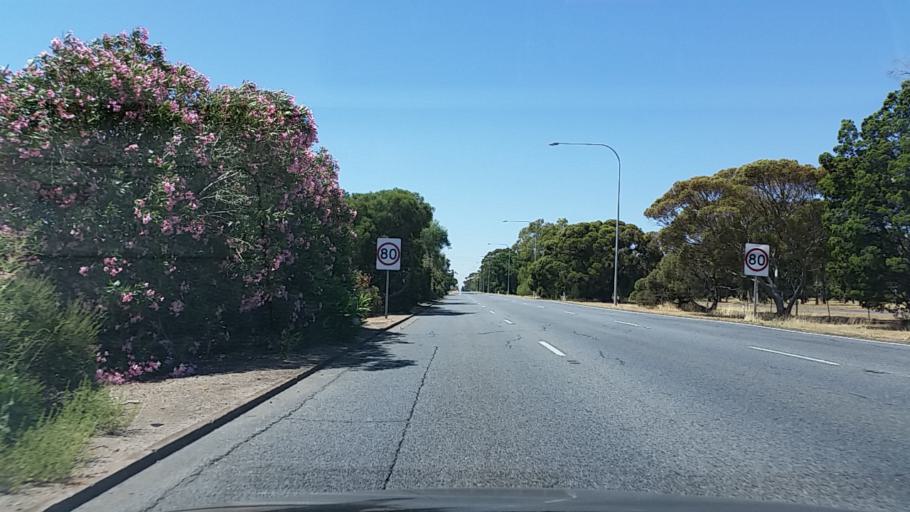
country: AU
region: South Australia
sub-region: Playford
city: Smithfield
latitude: -34.6987
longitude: 138.6837
